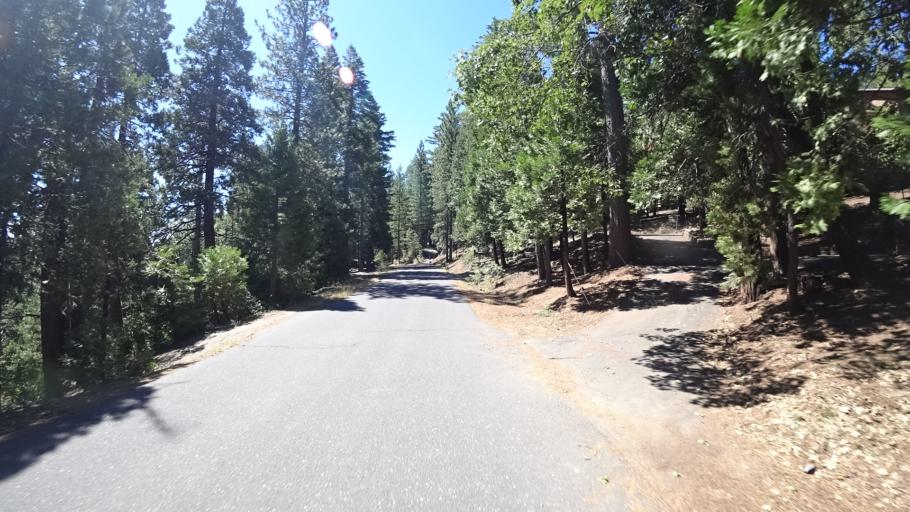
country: US
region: California
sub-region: Calaveras County
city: Arnold
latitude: 38.2884
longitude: -120.2871
